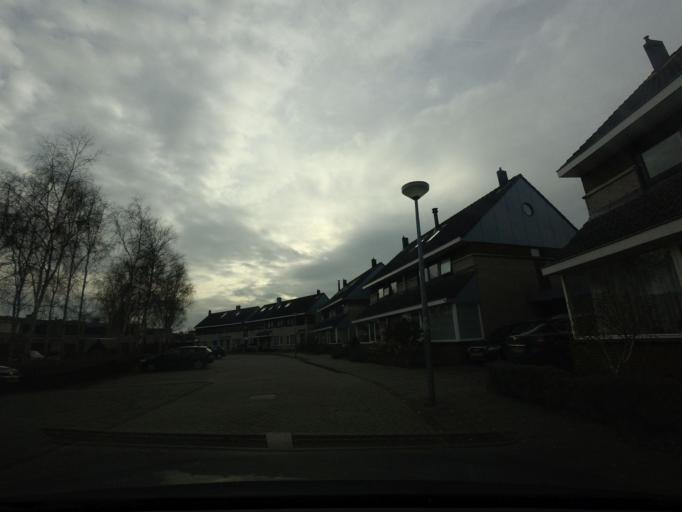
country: NL
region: North Holland
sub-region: Gemeente Alkmaar
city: Alkmaar
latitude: 52.6342
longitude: 4.7585
